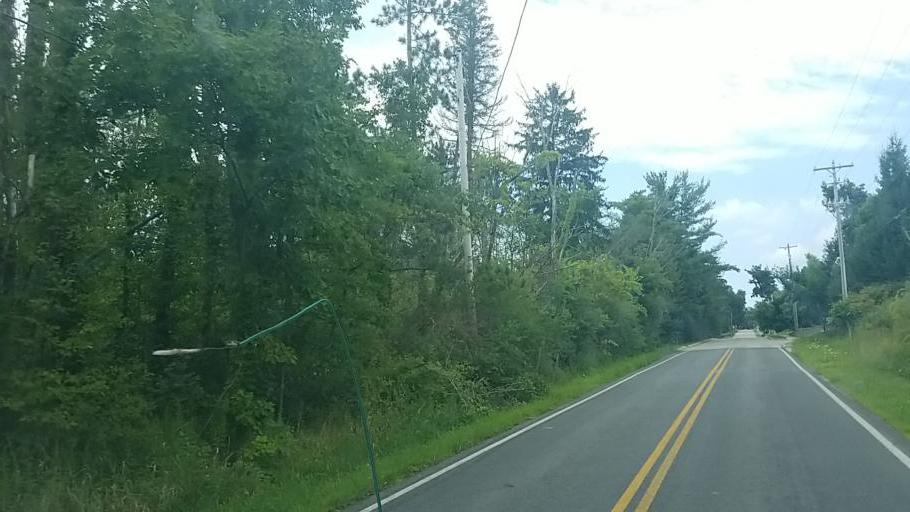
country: US
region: Ohio
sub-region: Medina County
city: Westfield Center
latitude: 41.0227
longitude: -81.9417
